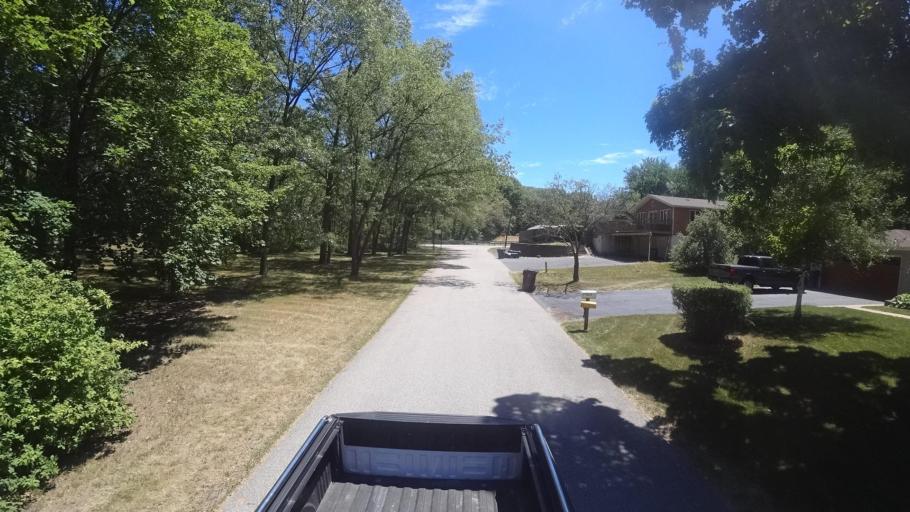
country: US
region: Indiana
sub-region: Porter County
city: Porter
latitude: 41.6400
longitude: -87.0633
